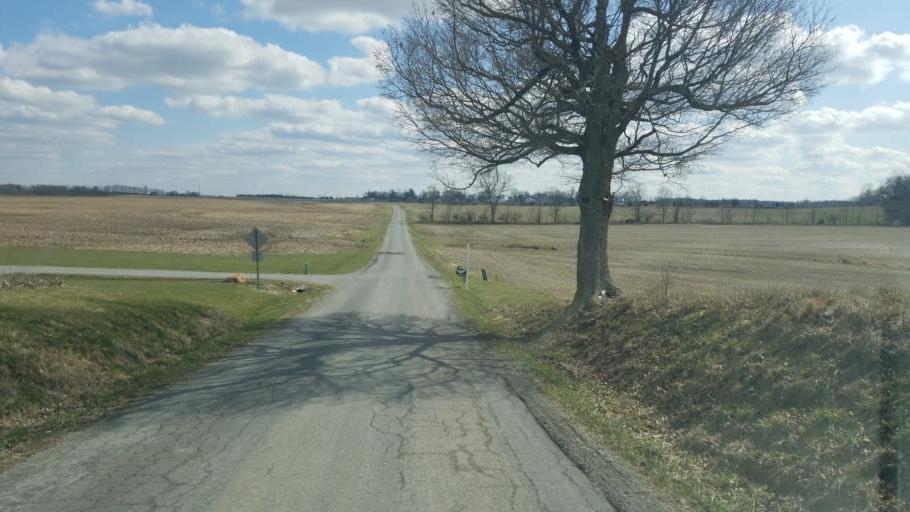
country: US
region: Ohio
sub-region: Highland County
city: Greenfield
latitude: 39.2730
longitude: -83.4457
